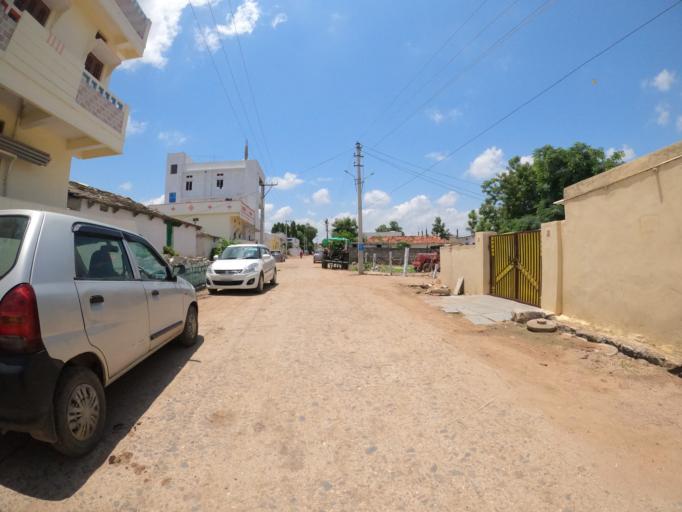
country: IN
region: Telangana
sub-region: Rangareddi
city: Singapur
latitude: 17.4403
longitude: 78.1585
